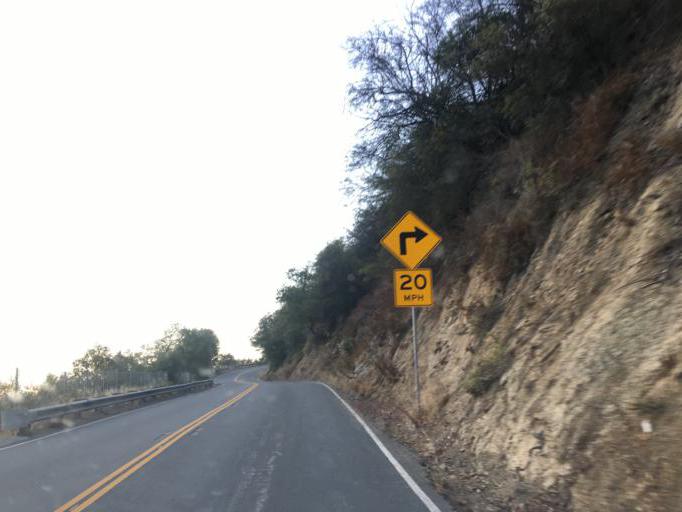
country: US
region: California
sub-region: Los Angeles County
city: Las Flores
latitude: 34.0668
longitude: -118.6448
